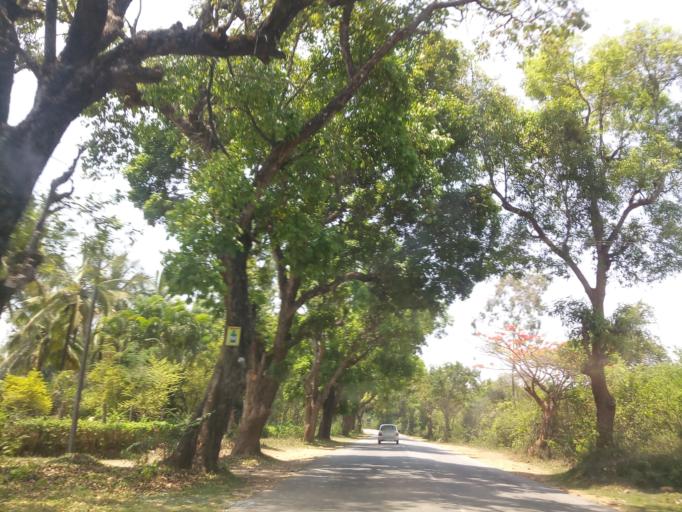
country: IN
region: Karnataka
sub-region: Hassan
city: Alur
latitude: 12.9539
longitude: 75.9099
